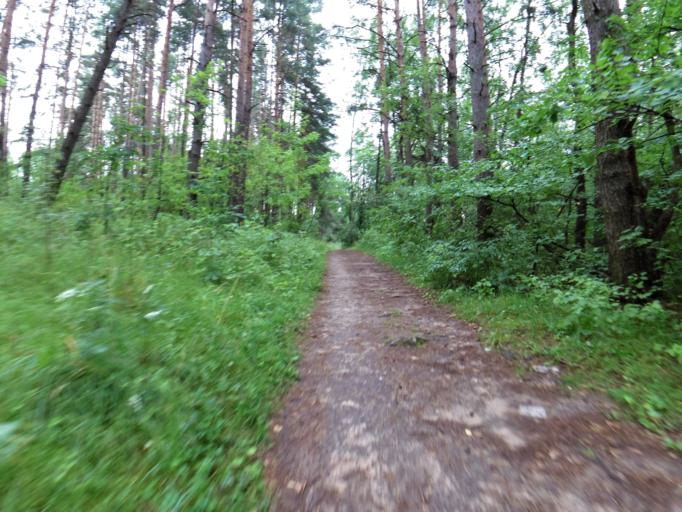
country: LT
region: Vilnius County
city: Pilaite
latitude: 54.6947
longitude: 25.2027
